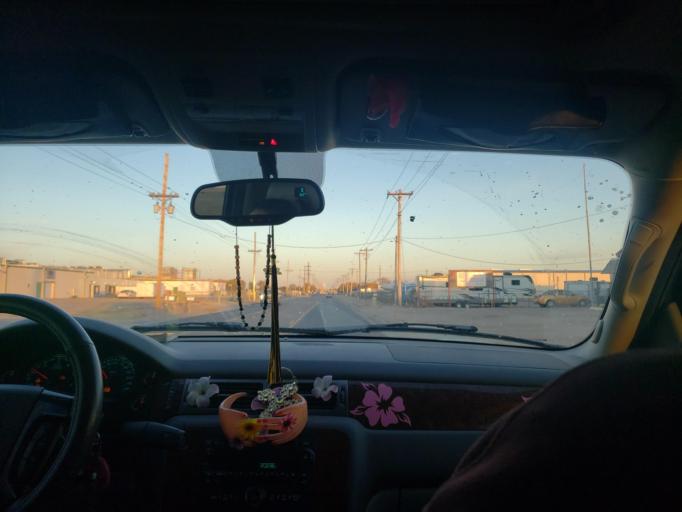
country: US
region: Kansas
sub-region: Finney County
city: Garden City
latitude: 37.9895
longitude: -100.8965
